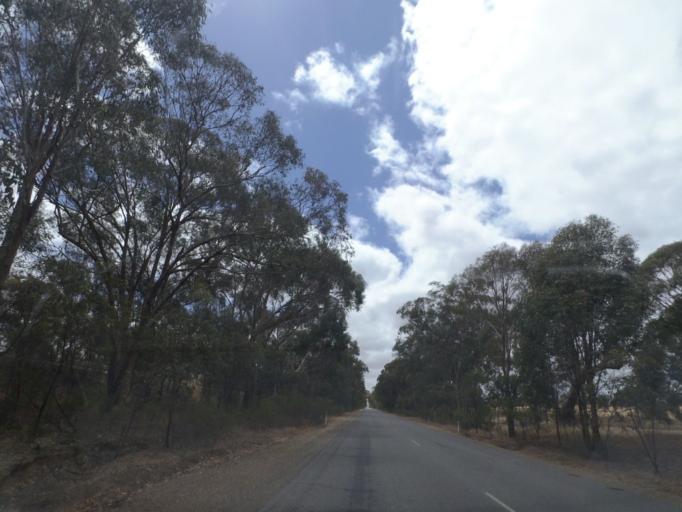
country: AU
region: Victoria
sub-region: Murrindindi
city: Kinglake West
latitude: -36.9266
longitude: 145.1907
